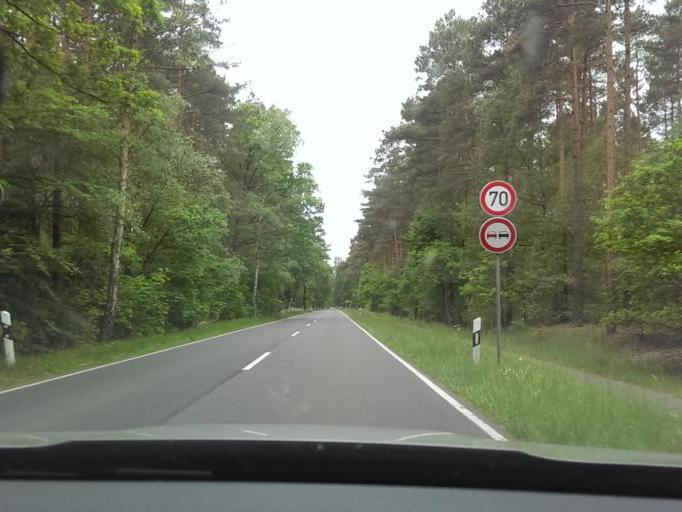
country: DE
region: Lower Saxony
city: Wietze
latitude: 52.6898
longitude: 9.8373
